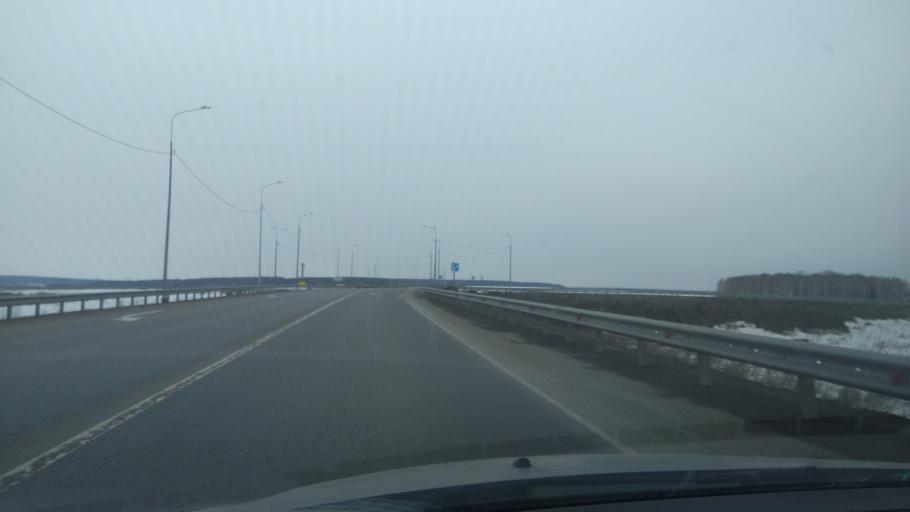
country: RU
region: Sverdlovsk
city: Achit
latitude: 56.7877
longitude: 57.8848
